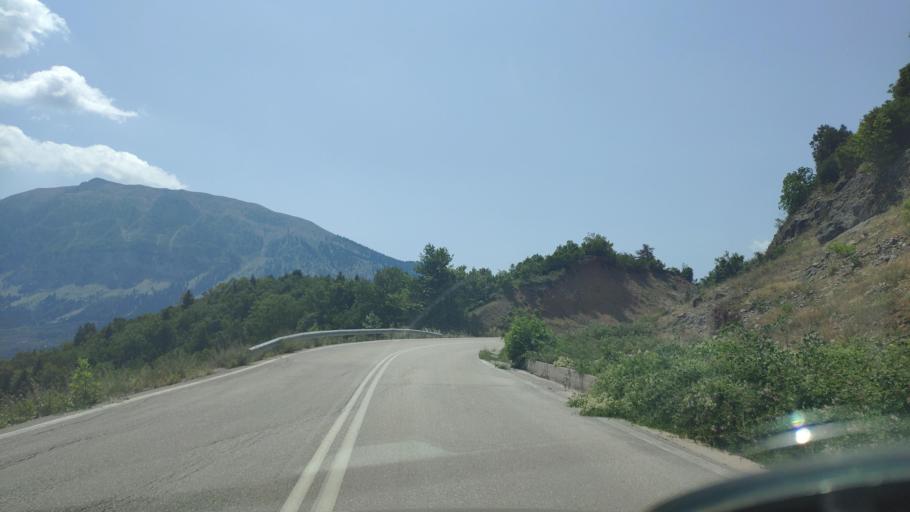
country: GR
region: Epirus
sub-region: Nomos Artas
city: Ano Kalentini
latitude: 39.2705
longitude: 21.3316
